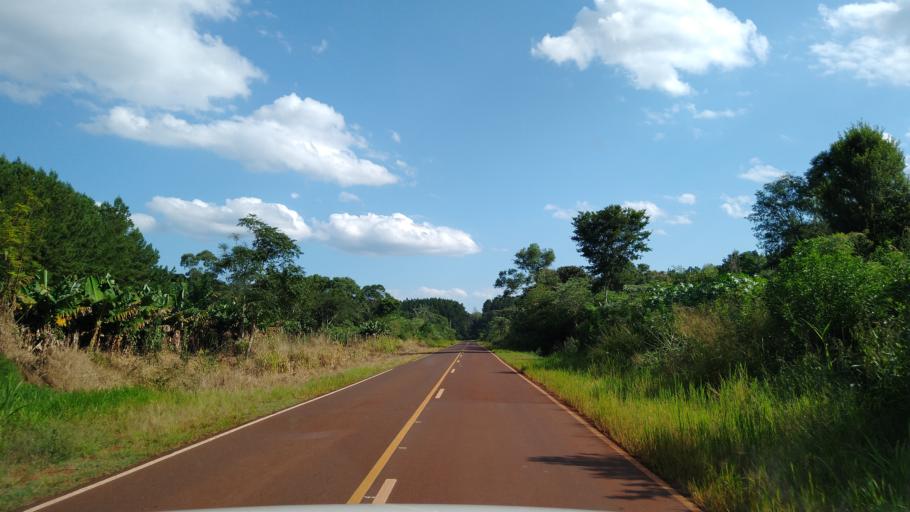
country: AR
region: Misiones
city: Puerto Piray
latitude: -26.4877
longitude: -54.6750
